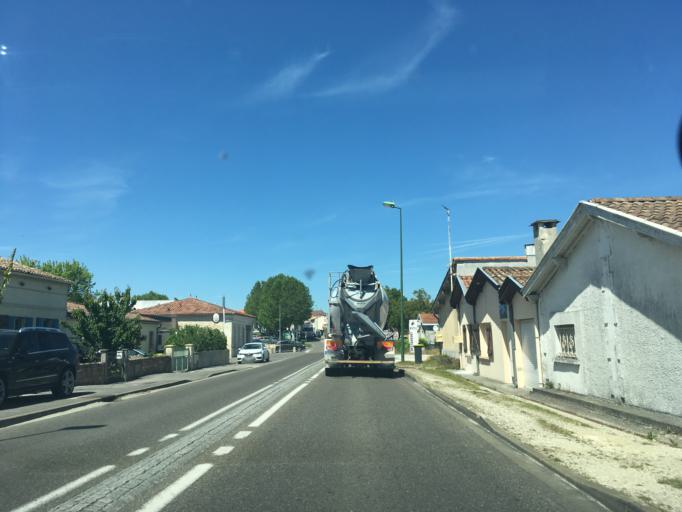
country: FR
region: Aquitaine
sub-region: Departement de la Gironde
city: Listrac-Medoc
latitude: 45.0722
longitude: -0.7930
